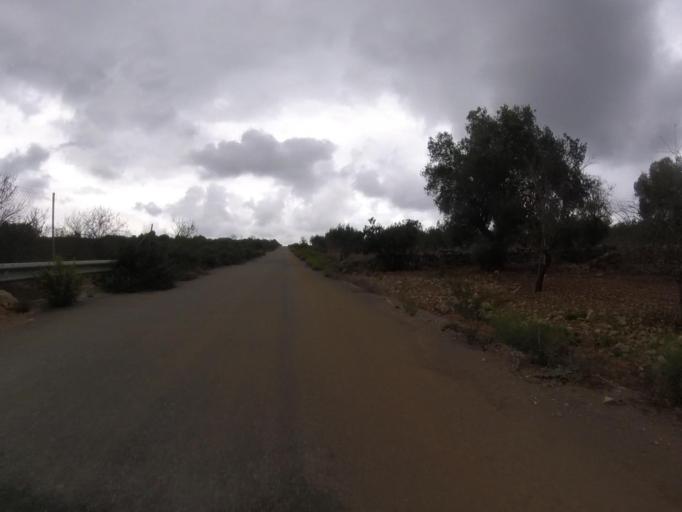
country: ES
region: Valencia
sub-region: Provincia de Castello
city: Benlloch
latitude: 40.2131
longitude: 0.0817
